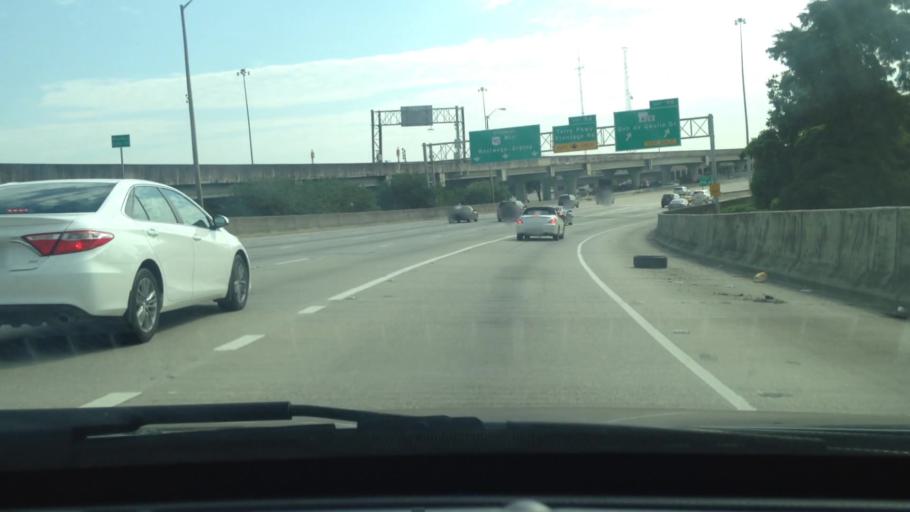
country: US
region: Louisiana
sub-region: Jefferson Parish
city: Gretna
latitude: 29.9366
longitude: -90.0394
